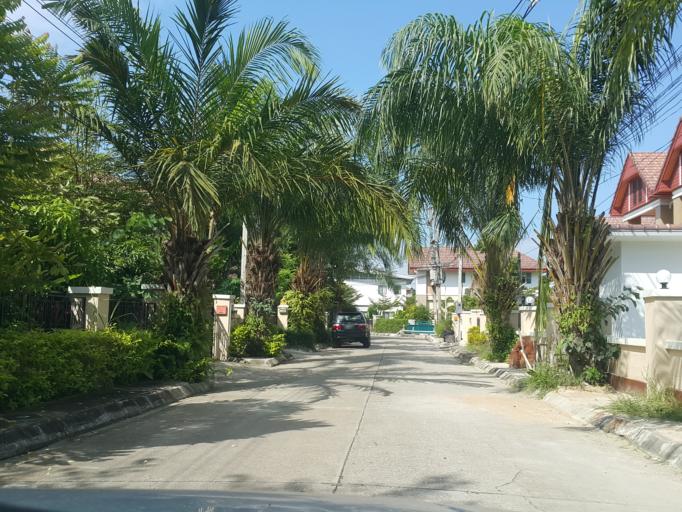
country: TH
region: Chiang Mai
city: Saraphi
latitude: 18.7370
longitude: 99.0476
